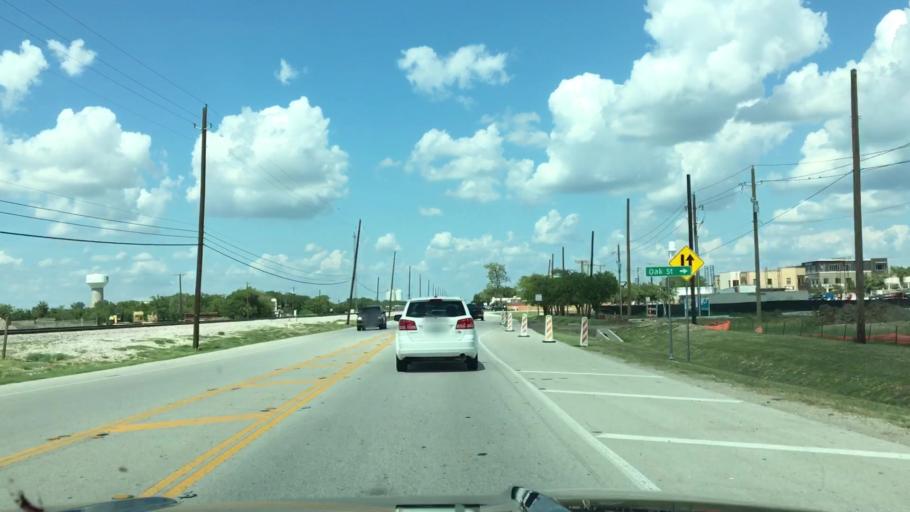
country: US
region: Texas
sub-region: Denton County
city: Roanoke
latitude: 32.9940
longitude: -97.2332
